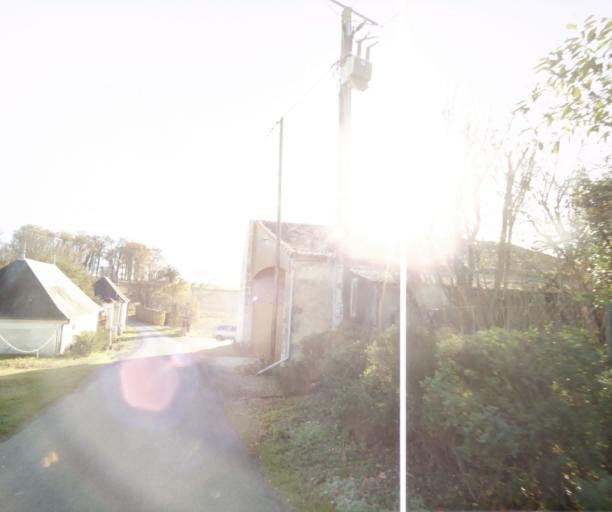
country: FR
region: Poitou-Charentes
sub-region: Departement de la Charente-Maritime
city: Chaniers
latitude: 45.7315
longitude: -0.5484
